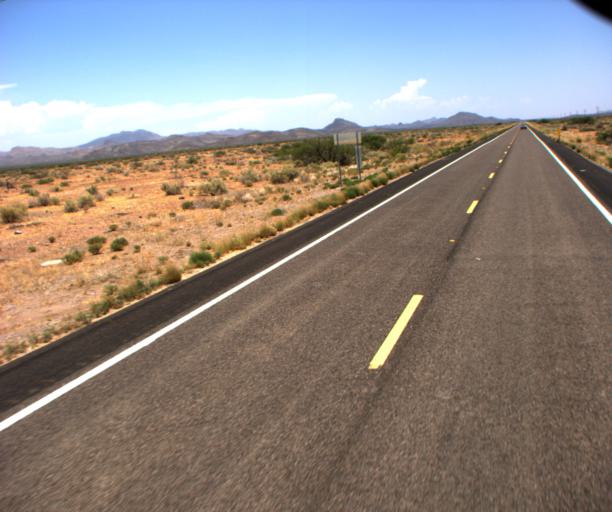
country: US
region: Arizona
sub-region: Graham County
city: Safford
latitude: 32.7737
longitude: -109.4954
